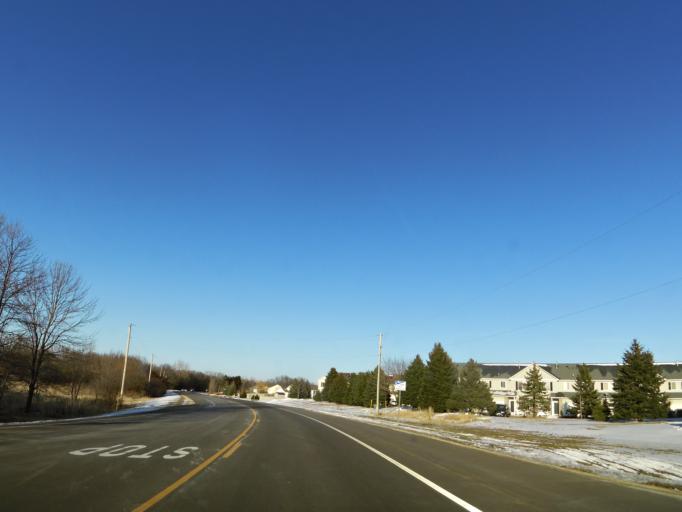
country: US
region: Minnesota
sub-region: Dakota County
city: Farmington
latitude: 44.6498
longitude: -93.1338
